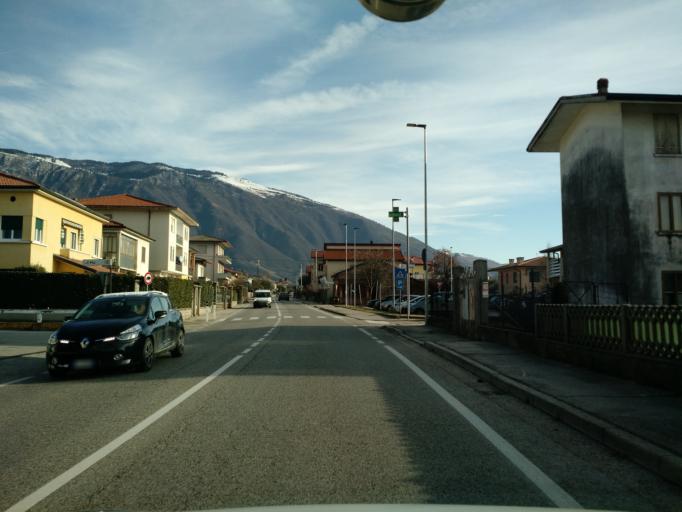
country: IT
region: Veneto
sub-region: Provincia di Vicenza
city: Piovene Rocchette
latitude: 45.7542
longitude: 11.4326
